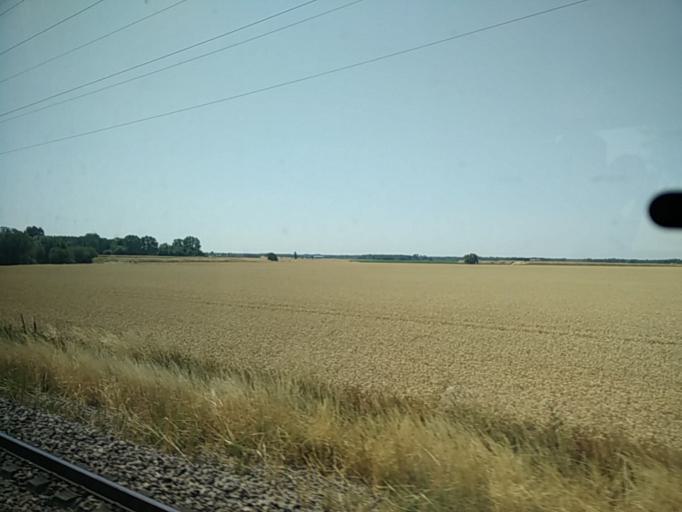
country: FR
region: Ile-de-France
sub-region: Departement de Seine-et-Marne
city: Bailly-Carrois
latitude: 48.5710
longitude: 2.9998
